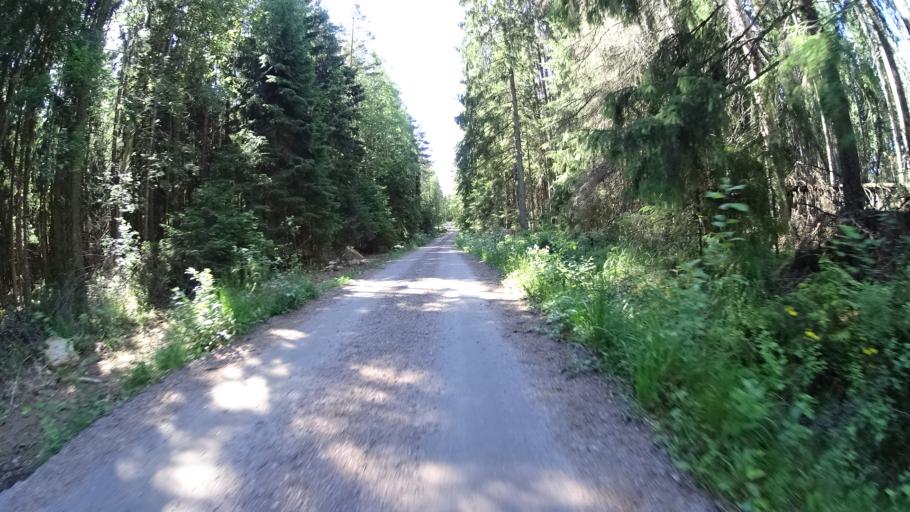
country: FI
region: Uusimaa
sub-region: Helsinki
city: Vihti
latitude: 60.3173
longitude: 24.4467
